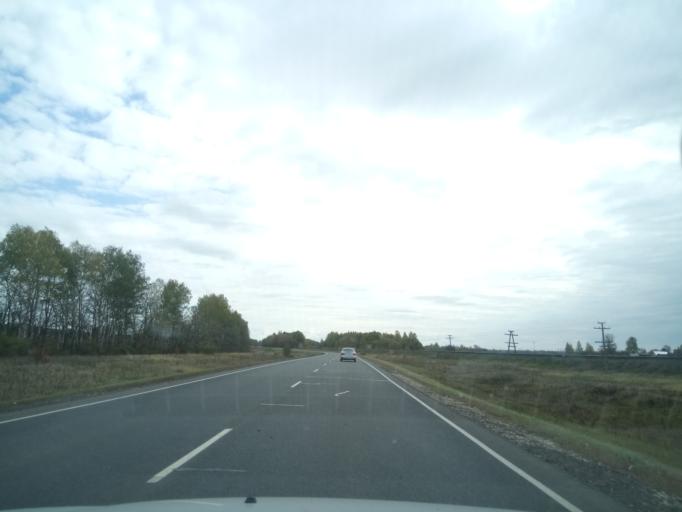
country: RU
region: Nizjnij Novgorod
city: Lukoyanov
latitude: 55.0667
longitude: 44.3473
